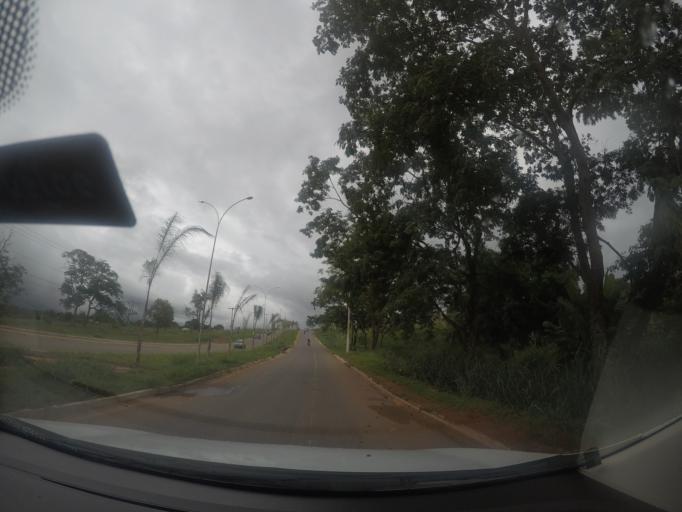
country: BR
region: Goias
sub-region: Trindade
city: Trindade
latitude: -16.6265
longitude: -49.3891
